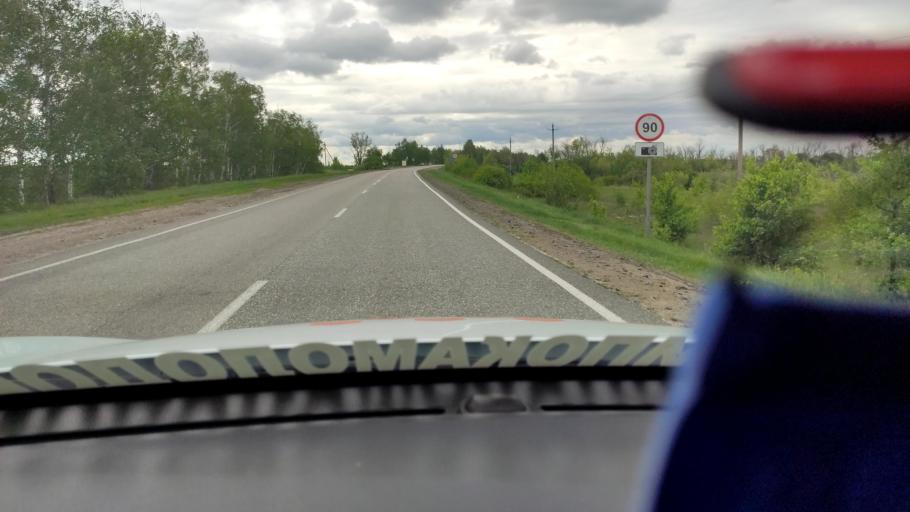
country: RU
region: Voronezj
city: Imeni Pervogo Maya
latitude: 50.7849
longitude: 39.3797
